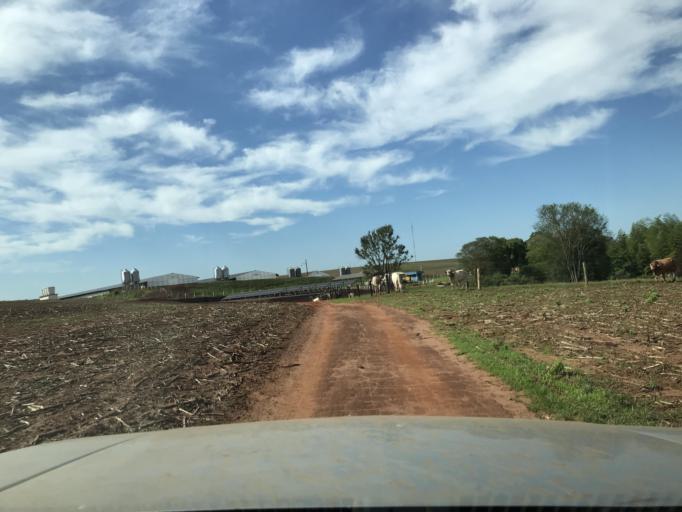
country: BR
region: Parana
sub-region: Palotina
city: Palotina
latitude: -24.1775
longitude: -53.8386
